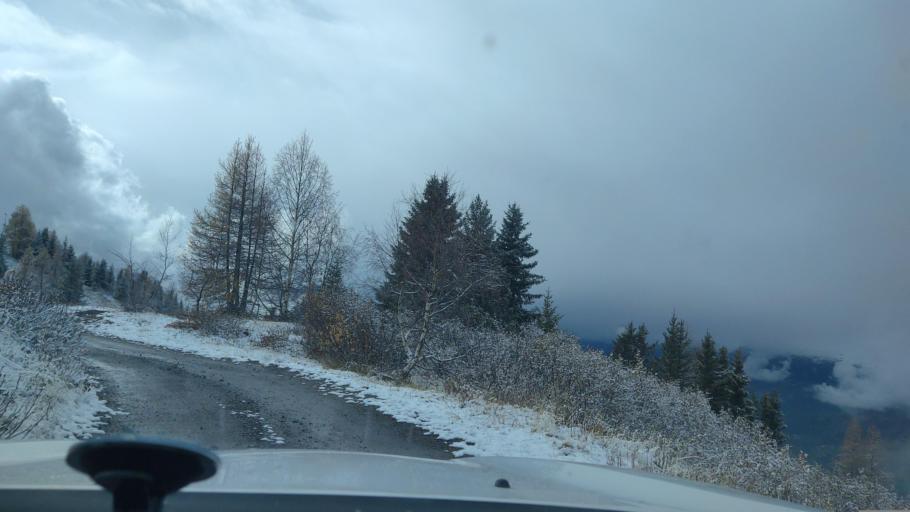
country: FR
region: Rhone-Alpes
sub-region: Departement de la Savoie
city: Seez
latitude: 45.5841
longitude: 6.8014
